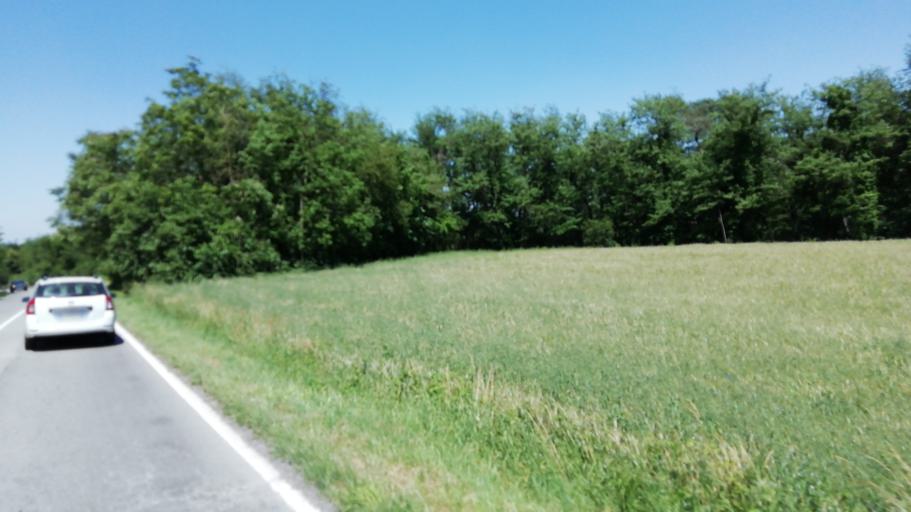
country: IT
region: Piedmont
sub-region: Provincia di Novara
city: Oleggio
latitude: 45.5901
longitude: 8.6791
